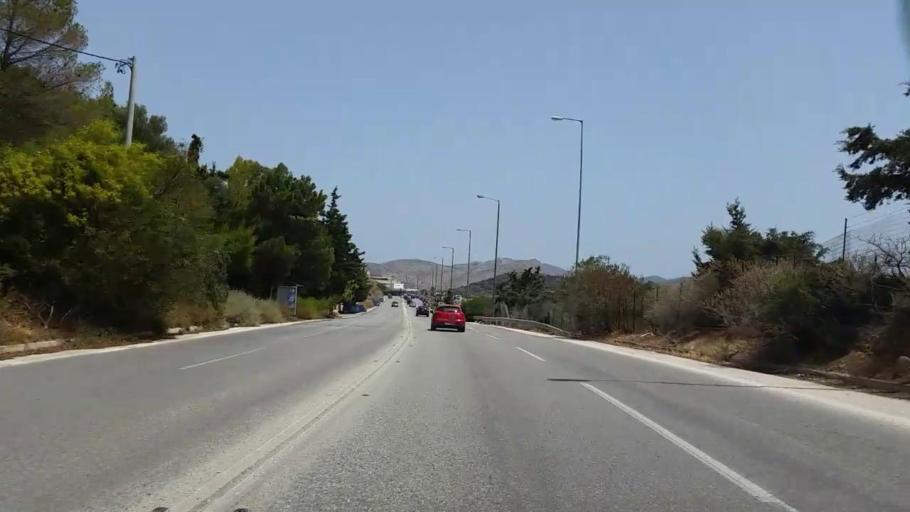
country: GR
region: Attica
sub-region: Nomarchia Anatolikis Attikis
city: Saronida
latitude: 37.7206
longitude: 23.9106
